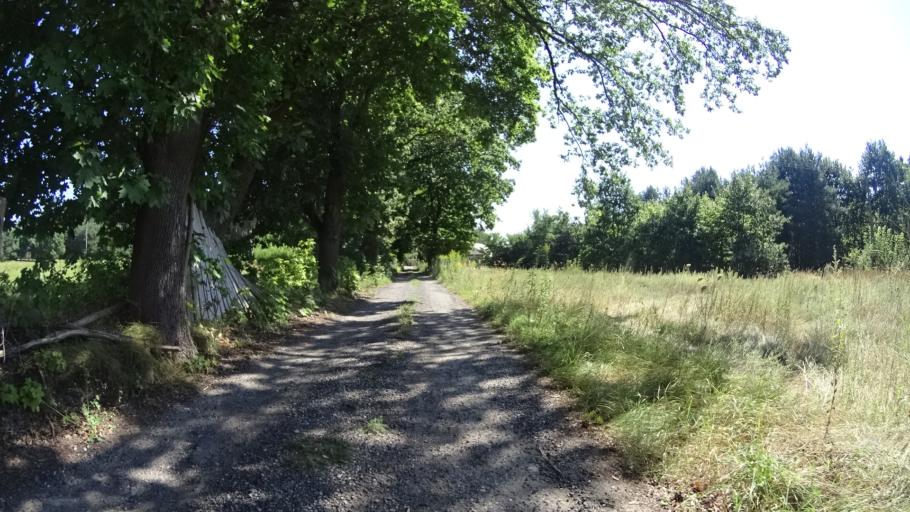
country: PL
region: Masovian Voivodeship
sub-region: Powiat bialobrzeski
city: Bialobrzegi
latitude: 51.6701
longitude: 20.9207
